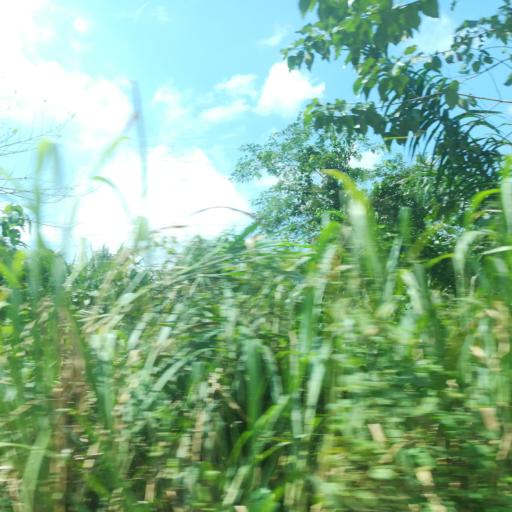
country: NG
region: Lagos
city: Ikorodu
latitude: 6.6600
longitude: 3.6819
